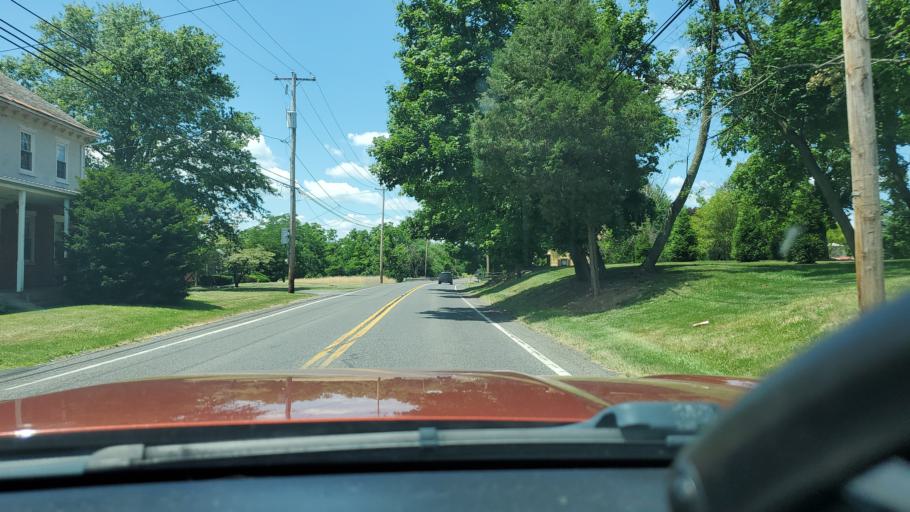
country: US
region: Pennsylvania
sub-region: Montgomery County
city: Limerick
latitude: 40.3031
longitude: -75.5298
